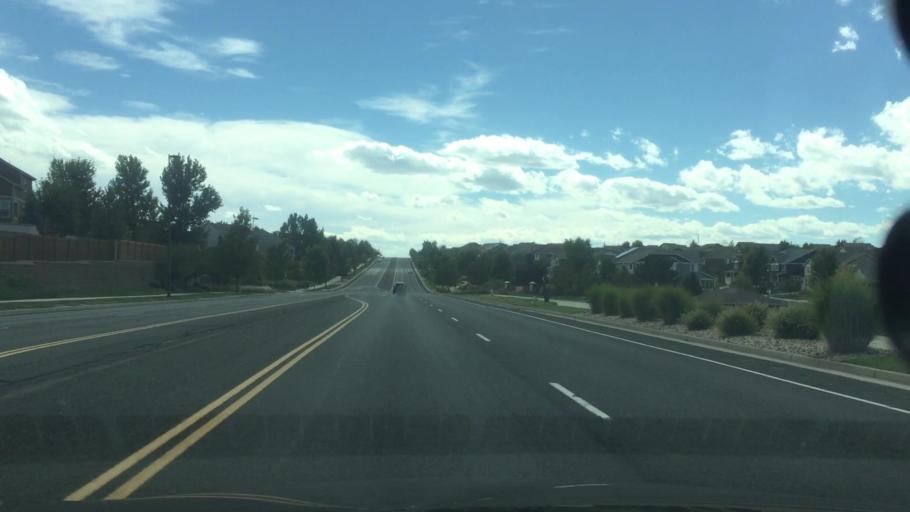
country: US
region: Colorado
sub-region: Arapahoe County
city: Dove Valley
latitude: 39.6477
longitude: -104.7351
